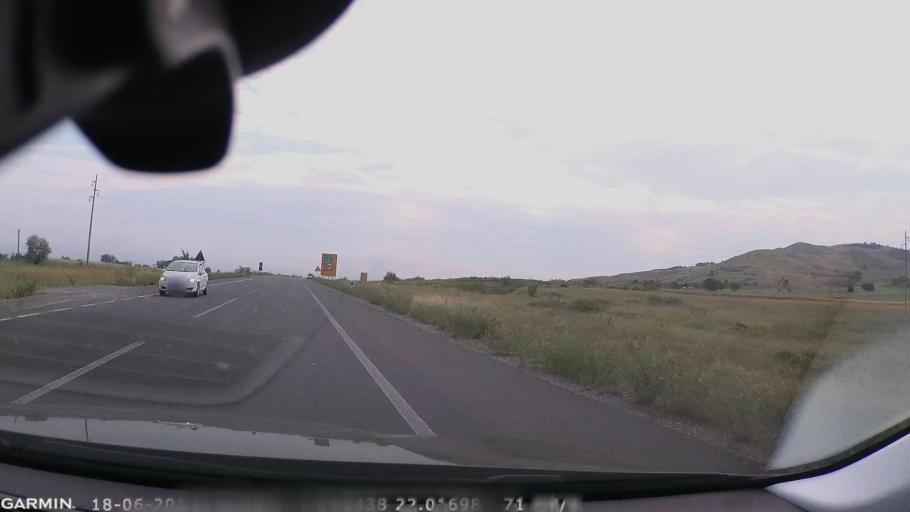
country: MK
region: Sveti Nikole
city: Sveti Nikole
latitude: 41.8029
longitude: 22.0142
